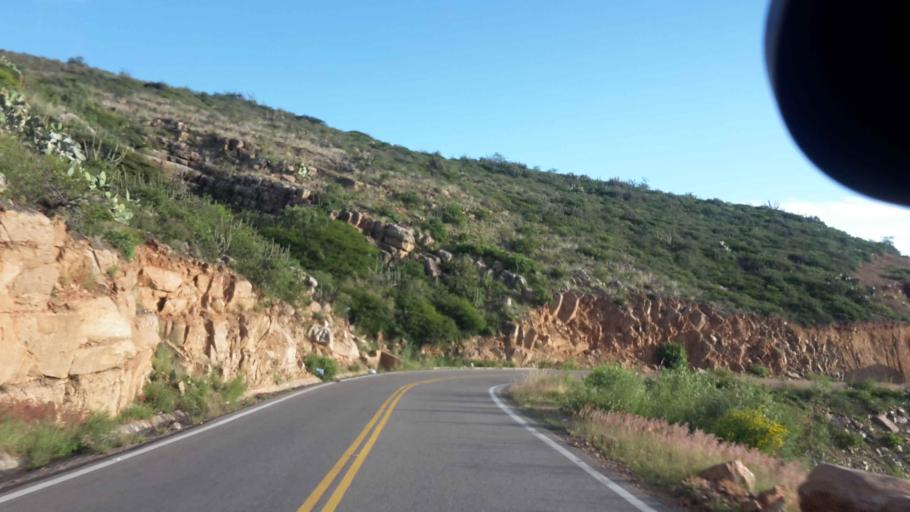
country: BO
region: Cochabamba
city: Arani
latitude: -17.5819
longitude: -65.7543
